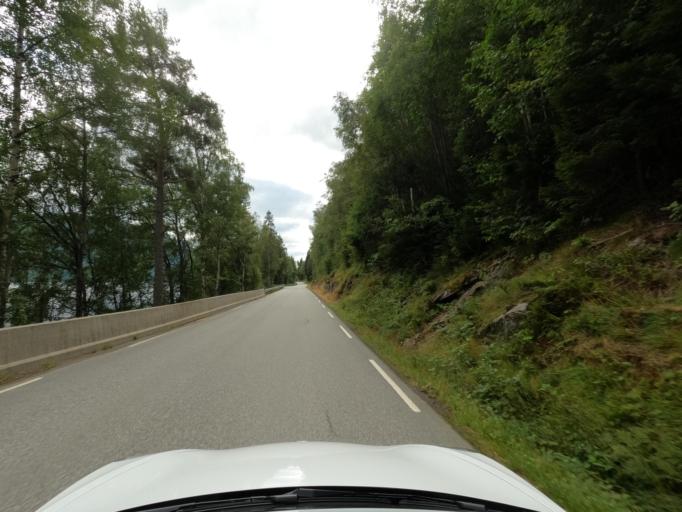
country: NO
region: Telemark
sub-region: Tinn
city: Rjukan
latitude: 59.9653
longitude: 8.8138
